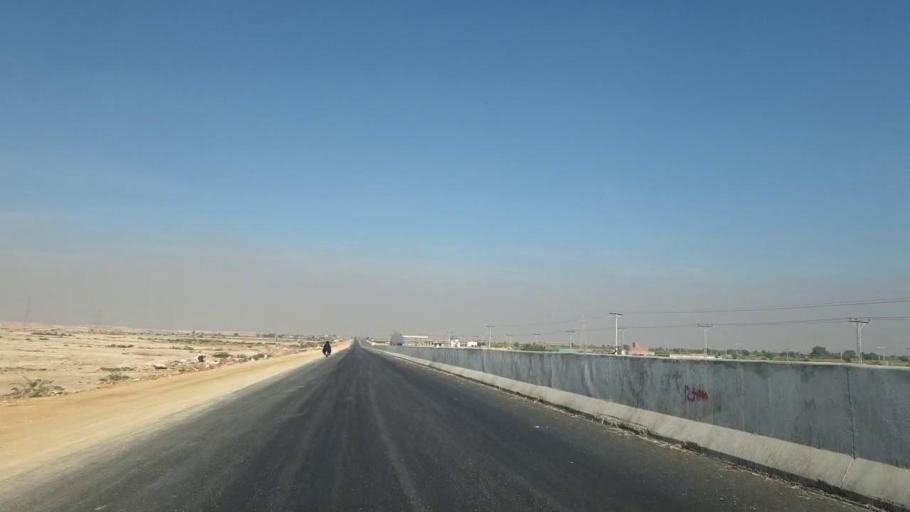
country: PK
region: Sindh
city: Jamshoro
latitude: 25.5090
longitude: 68.2734
